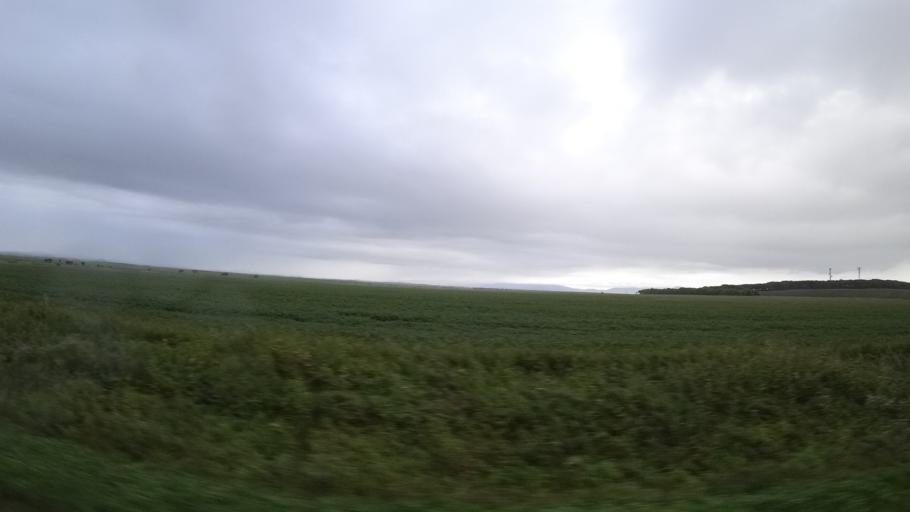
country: RU
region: Primorskiy
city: Chernigovka
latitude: 44.3758
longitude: 132.5297
